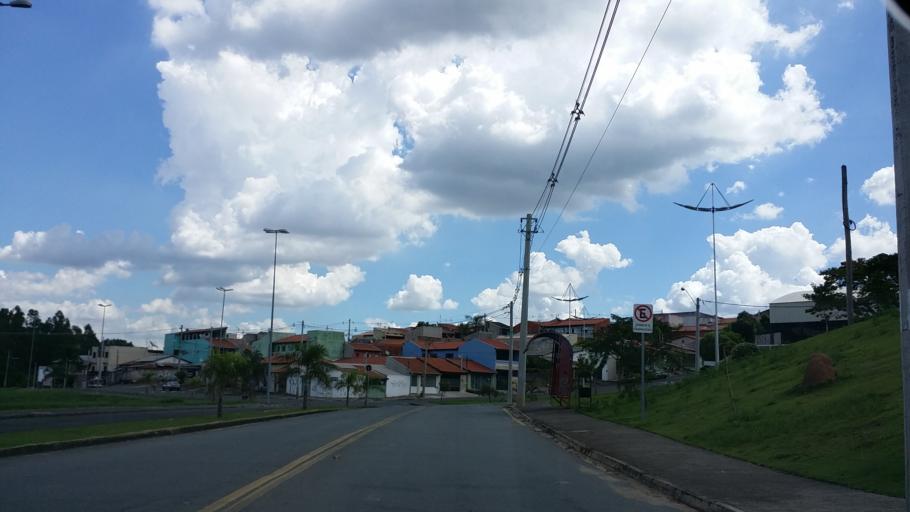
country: BR
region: Sao Paulo
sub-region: Indaiatuba
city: Indaiatuba
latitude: -23.1304
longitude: -47.2373
